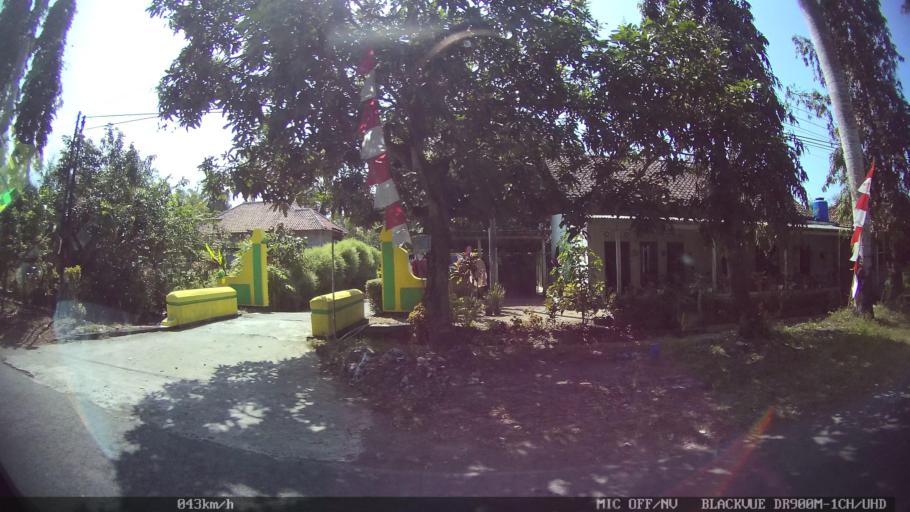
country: ID
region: Daerah Istimewa Yogyakarta
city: Srandakan
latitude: -7.9072
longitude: 110.1522
